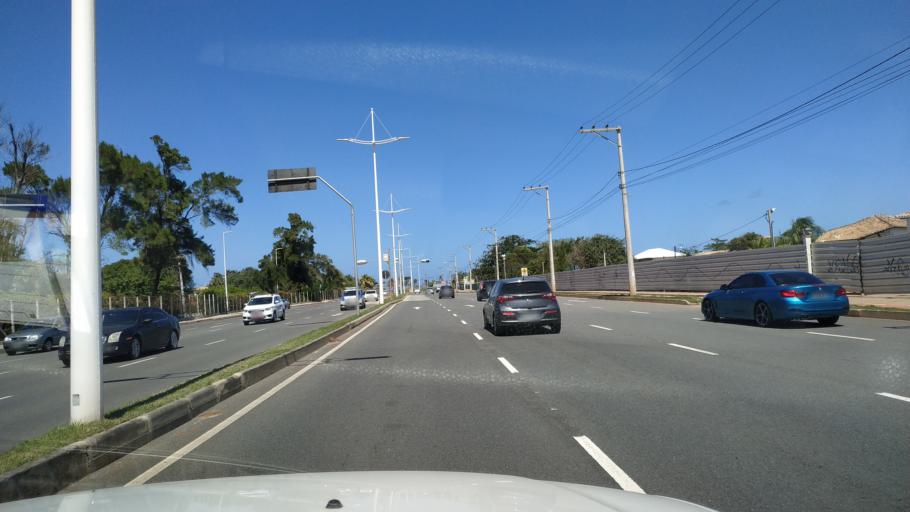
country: BR
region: Bahia
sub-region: Lauro De Freitas
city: Lauro de Freitas
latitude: -12.9505
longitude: -38.3848
